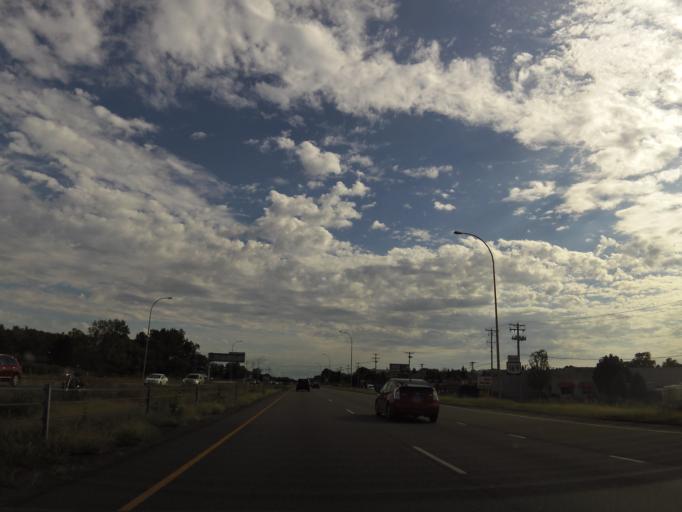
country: US
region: Minnesota
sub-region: Hennepin County
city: New Hope
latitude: 45.0548
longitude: -93.4010
